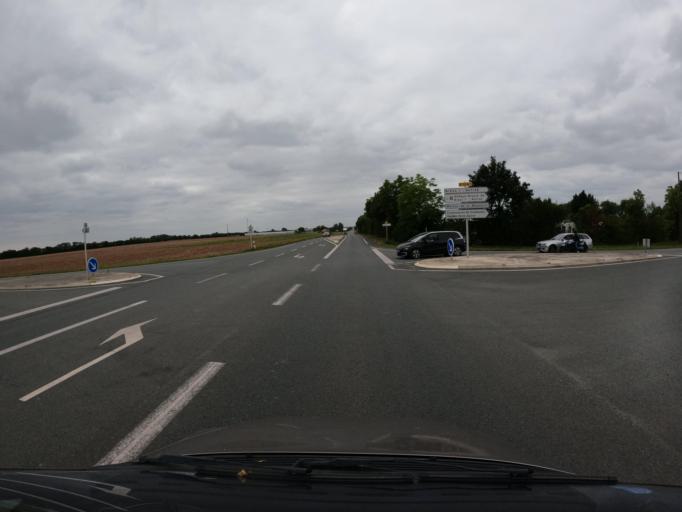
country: FR
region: Pays de la Loire
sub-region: Departement de la Vendee
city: Saint-Hilaire-des-Loges
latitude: 46.4062
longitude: -0.6784
